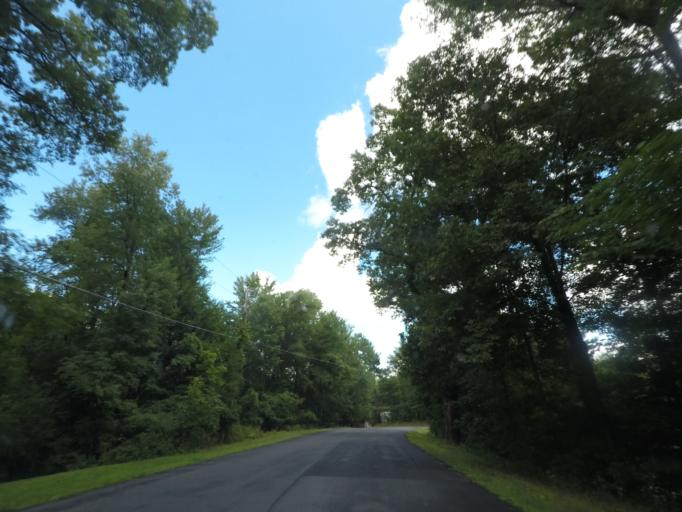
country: US
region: New York
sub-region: Rensselaer County
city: West Sand Lake
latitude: 42.6558
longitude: -73.5998
